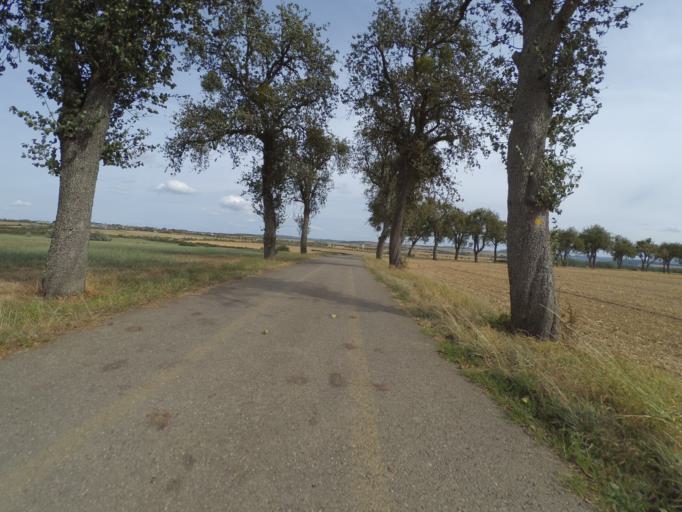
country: LU
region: Grevenmacher
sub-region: Canton de Remich
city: Mondorf-les-Bains
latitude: 49.5021
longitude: 6.2957
